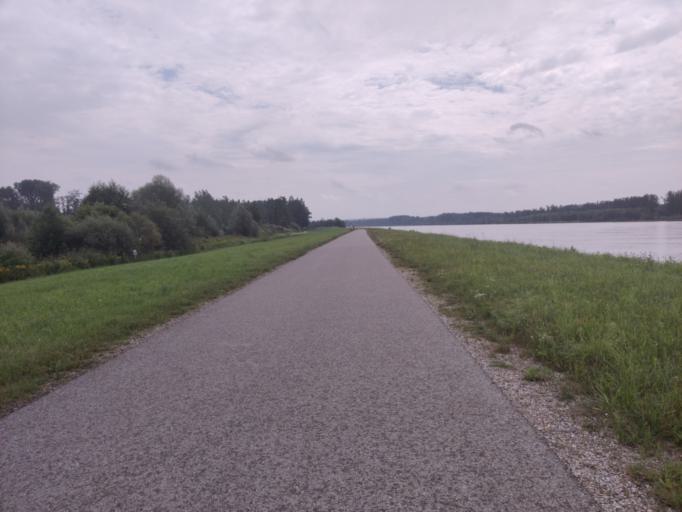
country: AT
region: Upper Austria
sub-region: Politischer Bezirk Perg
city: Perg
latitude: 48.2079
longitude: 14.6019
